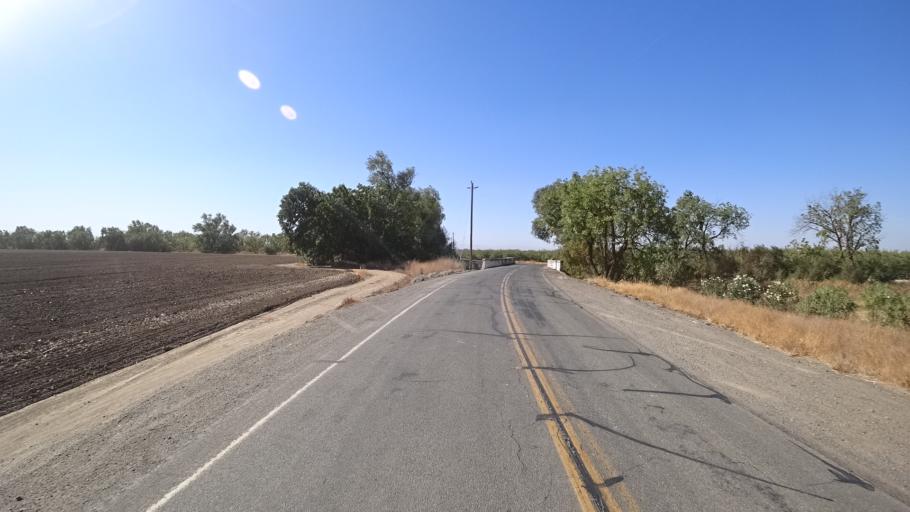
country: US
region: California
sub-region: Yolo County
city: Davis
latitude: 38.5907
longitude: -121.8157
